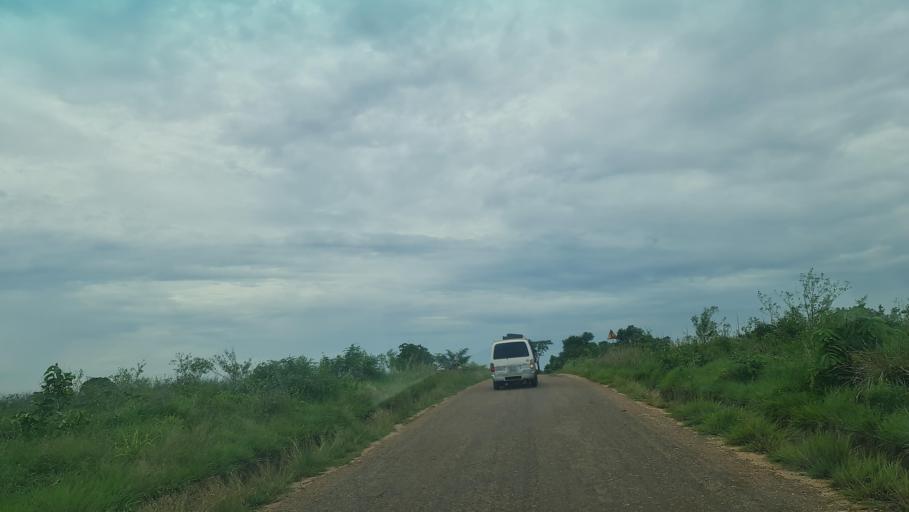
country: MW
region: Southern Region
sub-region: Nsanje District
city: Nsanje
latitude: -17.6823
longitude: 35.7258
